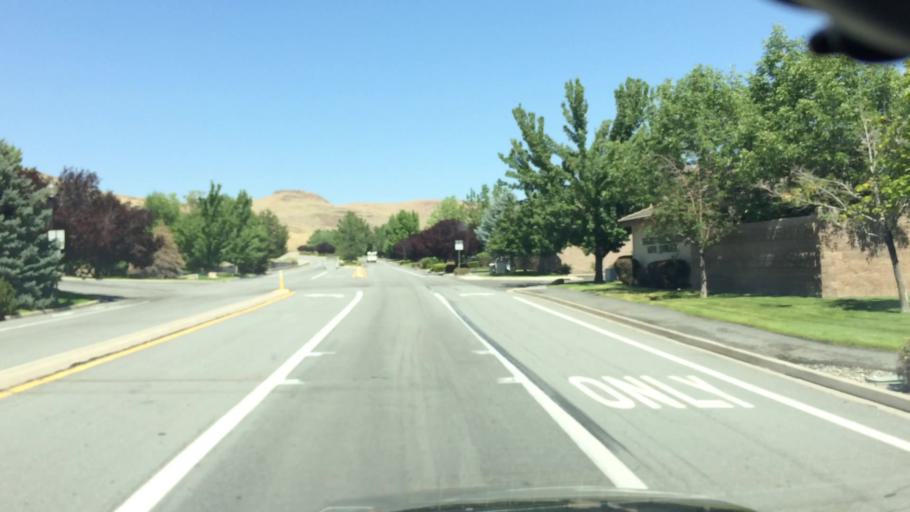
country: US
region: Nevada
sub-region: Washoe County
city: Sparks
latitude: 39.5648
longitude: -119.7040
